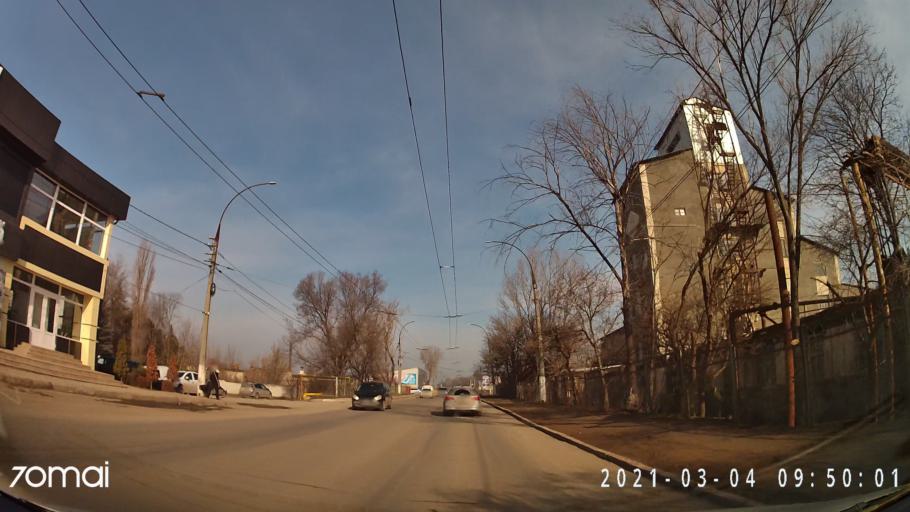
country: MD
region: Balti
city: Balti
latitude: 47.7693
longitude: 27.9303
